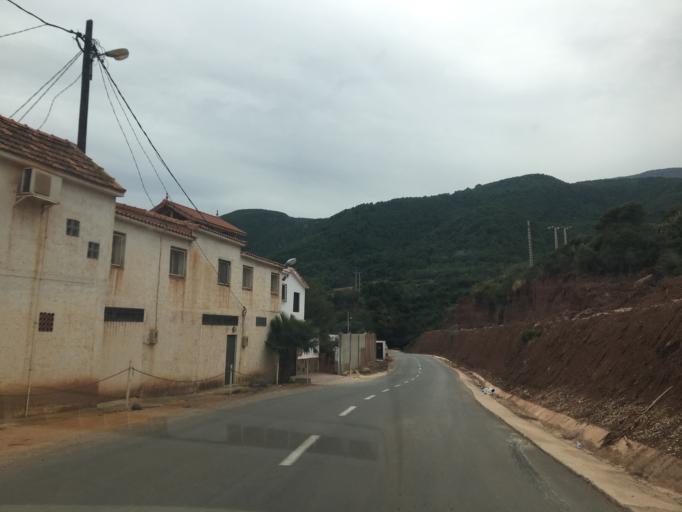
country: DZ
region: Tipaza
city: Tipasa
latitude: 36.6296
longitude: 2.4013
